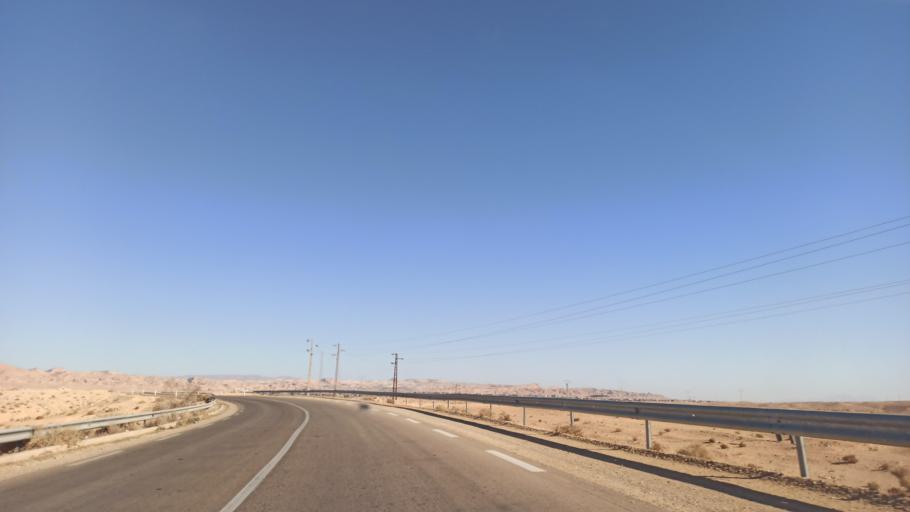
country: TN
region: Gafsa
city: Al Metlaoui
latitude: 34.2986
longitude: 8.3588
